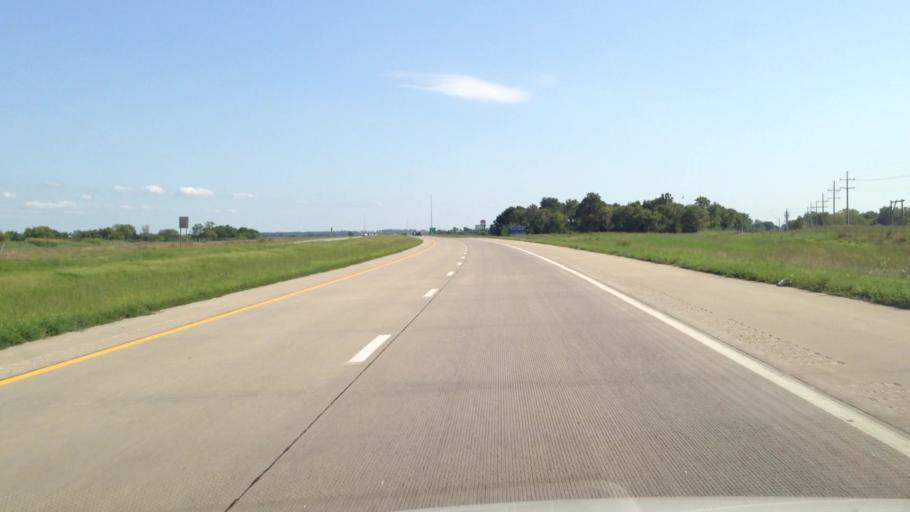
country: US
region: Kansas
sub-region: Linn County
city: Pleasanton
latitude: 38.1924
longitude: -94.7066
